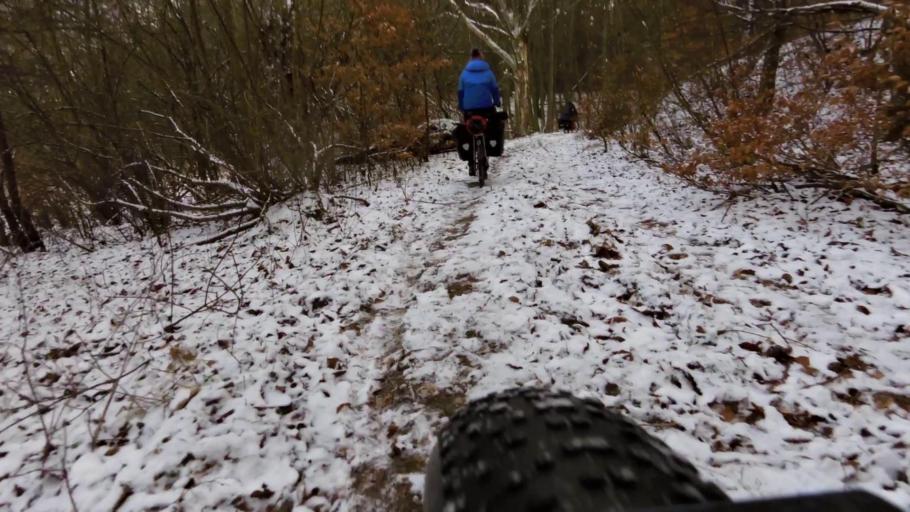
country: PL
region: West Pomeranian Voivodeship
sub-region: Powiat walecki
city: Tuczno
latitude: 53.2995
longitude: 16.2881
